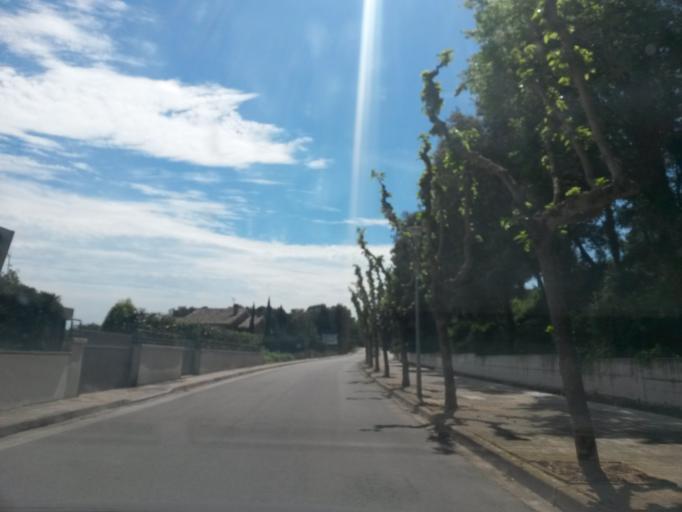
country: ES
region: Catalonia
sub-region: Provincia de Girona
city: Vilablareix
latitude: 41.9654
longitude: 2.7625
